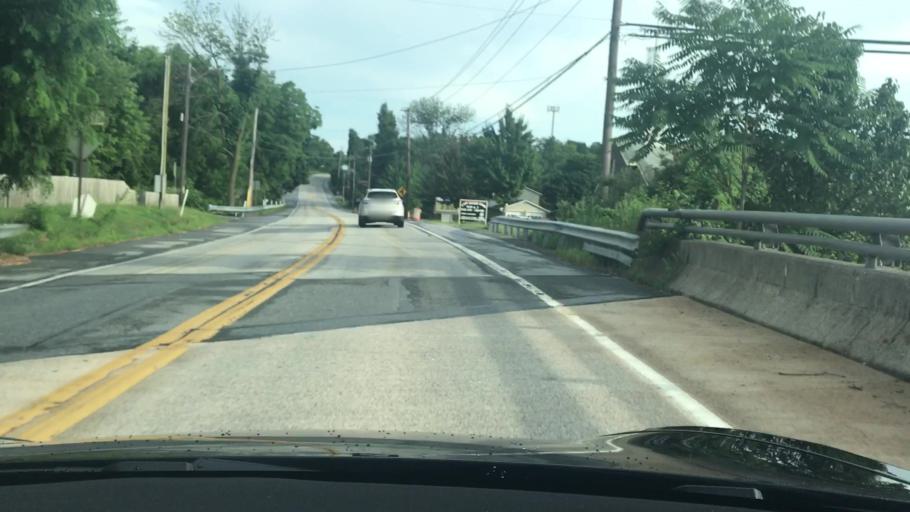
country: US
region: Pennsylvania
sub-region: Dauphin County
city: Colonial Park
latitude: 40.3182
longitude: -76.8236
